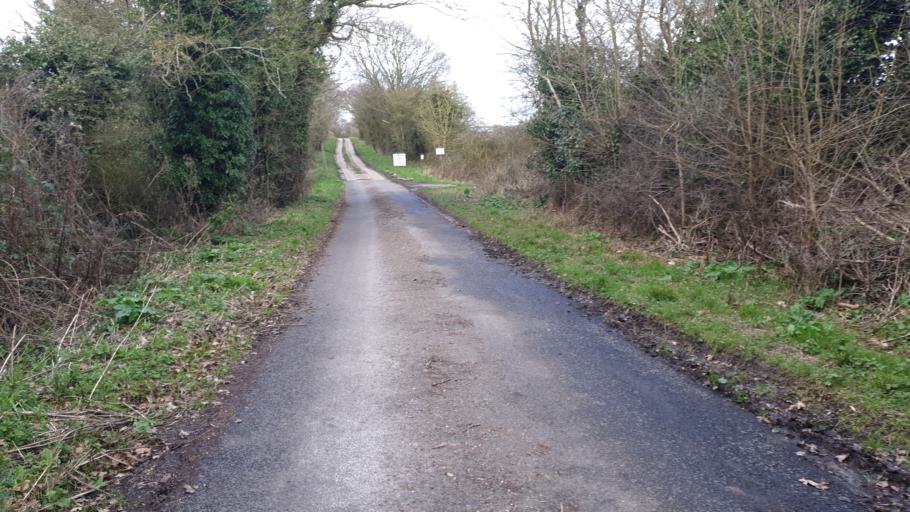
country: GB
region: England
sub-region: Essex
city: Little Clacton
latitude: 51.8292
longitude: 1.1727
